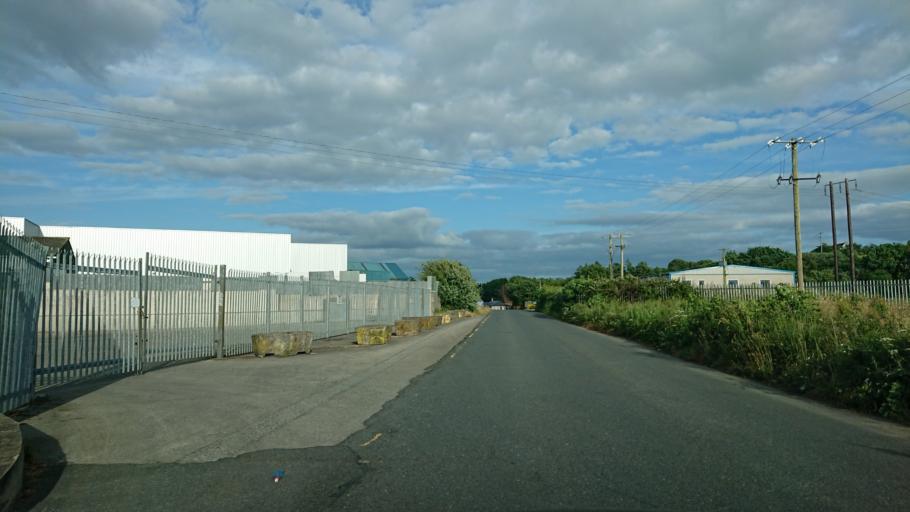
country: IE
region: Munster
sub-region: Waterford
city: Waterford
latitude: 52.2421
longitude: -7.1608
